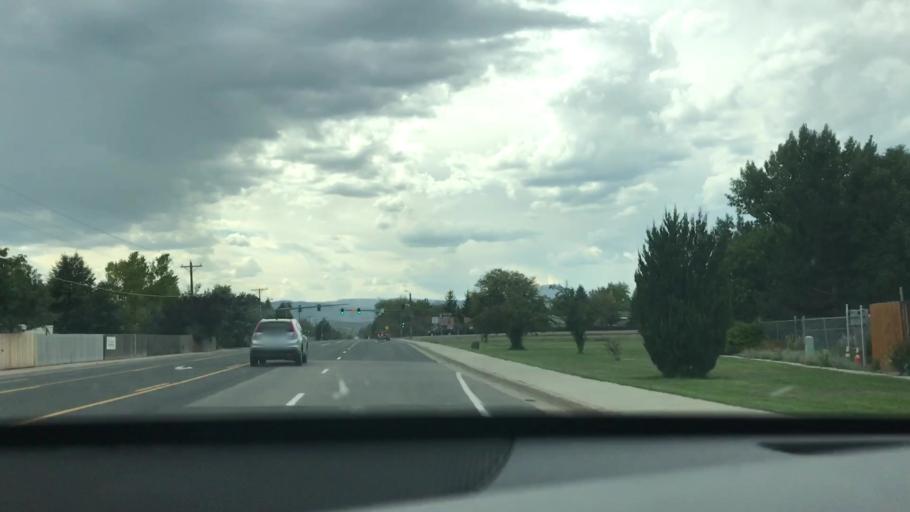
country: US
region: Colorado
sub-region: Larimer County
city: Loveland
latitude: 40.3785
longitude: -105.1139
